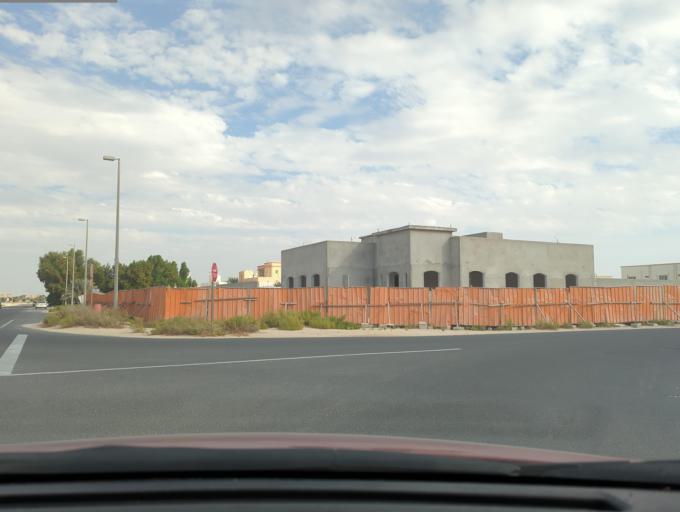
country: AE
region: Abu Dhabi
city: Abu Dhabi
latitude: 24.3846
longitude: 54.7013
